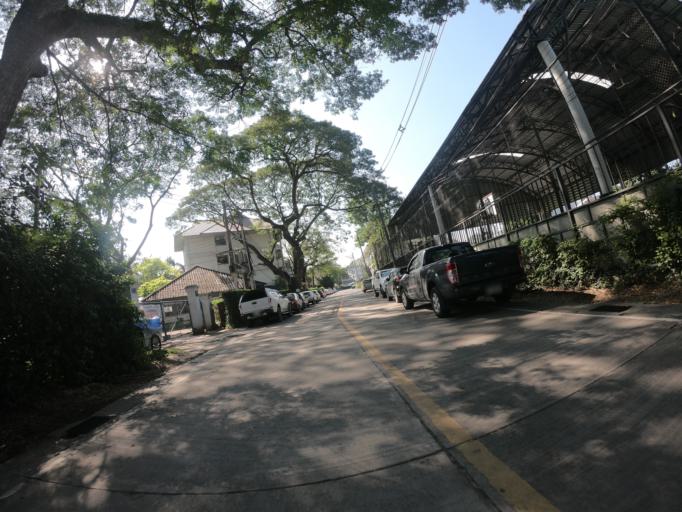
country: TH
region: Chiang Mai
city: Chiang Mai
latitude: 18.7990
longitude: 99.0055
